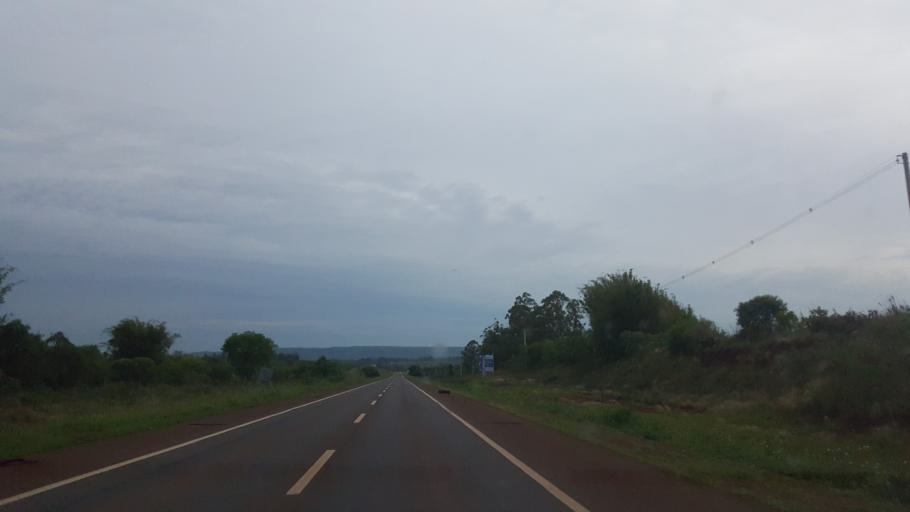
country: AR
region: Misiones
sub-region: Departamento de Apostoles
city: San Jose
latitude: -27.7760
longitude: -55.8093
